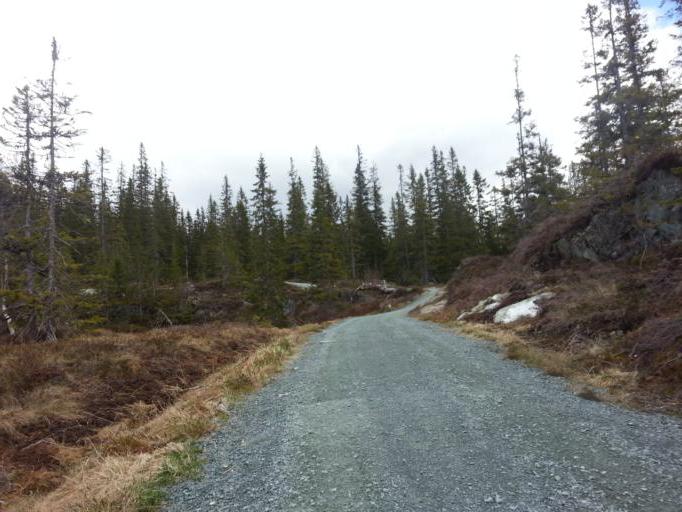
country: NO
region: Nord-Trondelag
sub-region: Levanger
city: Skogn
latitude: 63.5872
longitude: 11.0882
